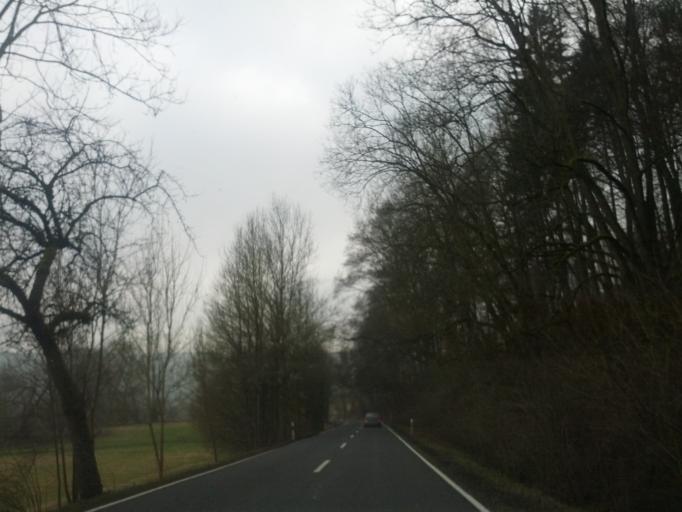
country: DE
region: Thuringia
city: Creuzburg
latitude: 51.0689
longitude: 10.2646
